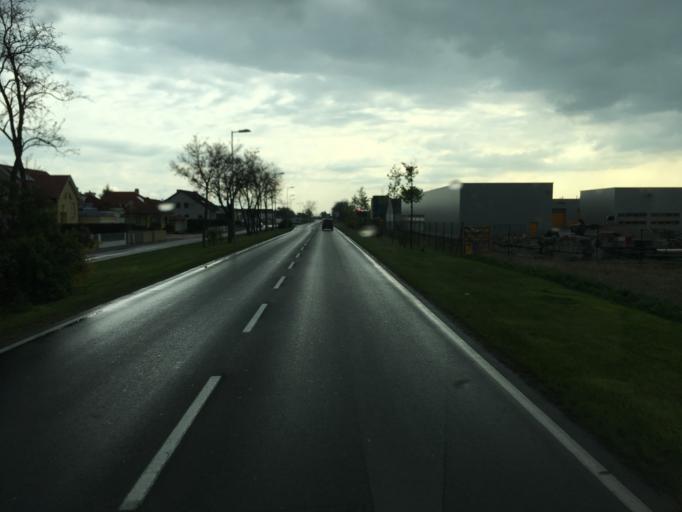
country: AT
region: Burgenland
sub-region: Politischer Bezirk Neusiedl am See
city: Parndorf
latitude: 47.9989
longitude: 16.8689
